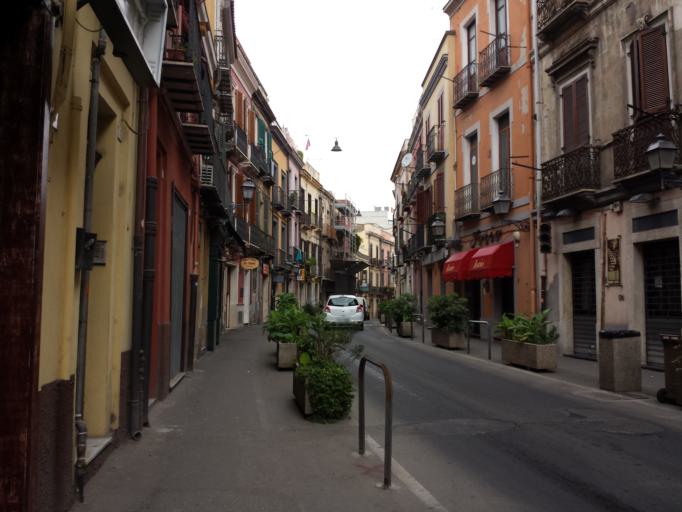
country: IT
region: Sardinia
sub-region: Provincia di Cagliari
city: Cagliari
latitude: 39.2183
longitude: 9.1109
